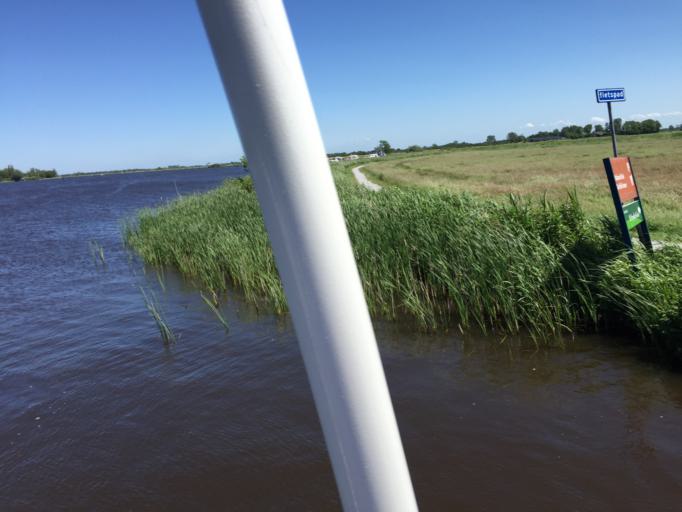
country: NL
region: Friesland
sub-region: Gemeente Smallingerland
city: Oudega
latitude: 53.1020
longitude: 5.9490
